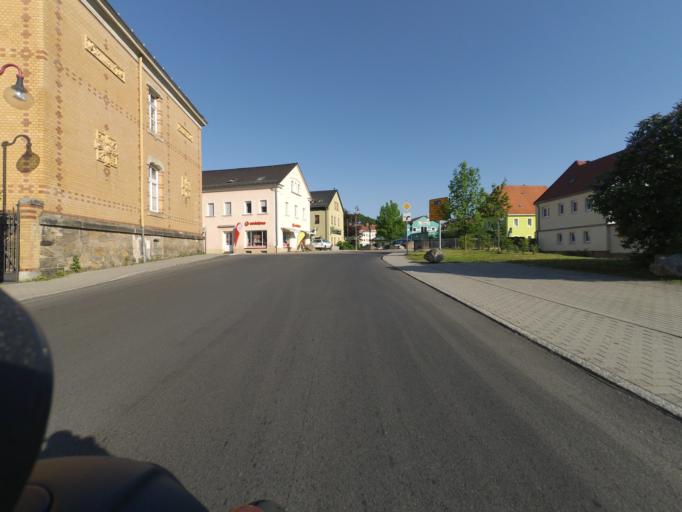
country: DE
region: Saxony
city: Dippoldiswalde
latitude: 50.8940
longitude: 13.6652
